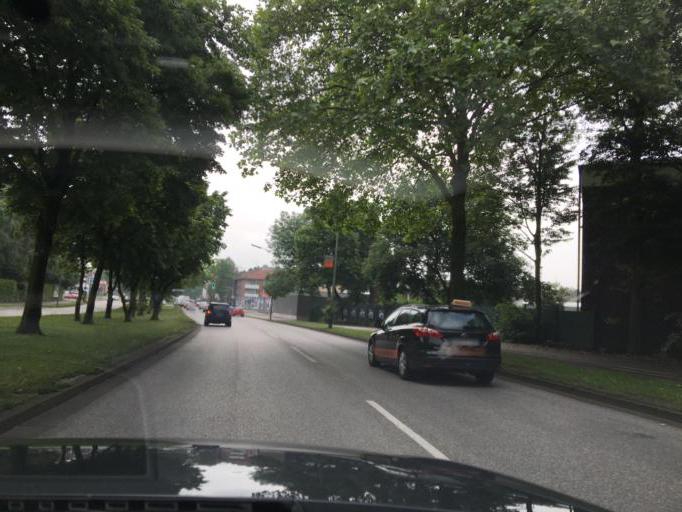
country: DE
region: North Rhine-Westphalia
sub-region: Regierungsbezirk Munster
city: Gelsenkirchen
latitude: 51.5198
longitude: 7.0784
